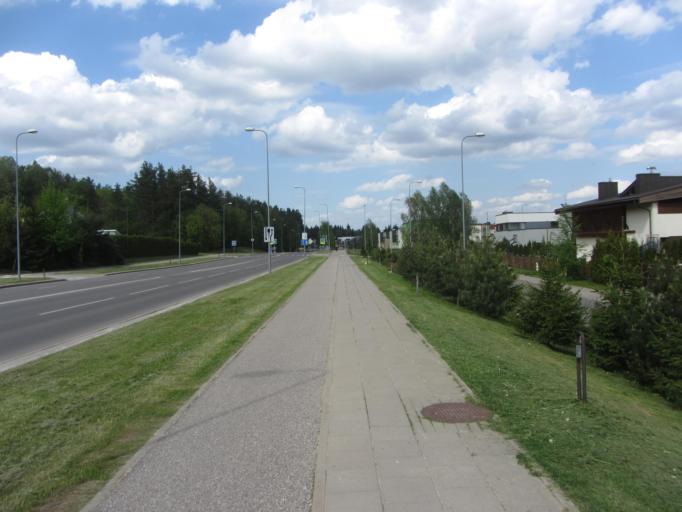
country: LT
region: Vilnius County
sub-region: Vilnius
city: Fabijoniskes
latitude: 54.7596
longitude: 25.2817
